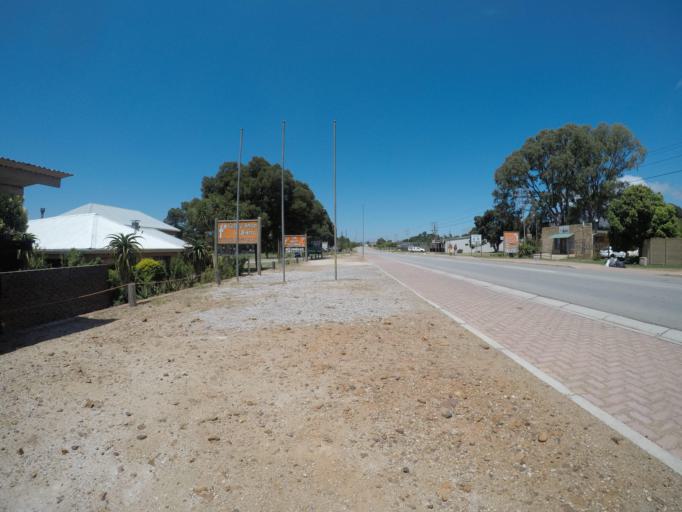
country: ZA
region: Eastern Cape
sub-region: Cacadu District Municipality
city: Kareedouw
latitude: -33.9517
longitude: 24.2906
